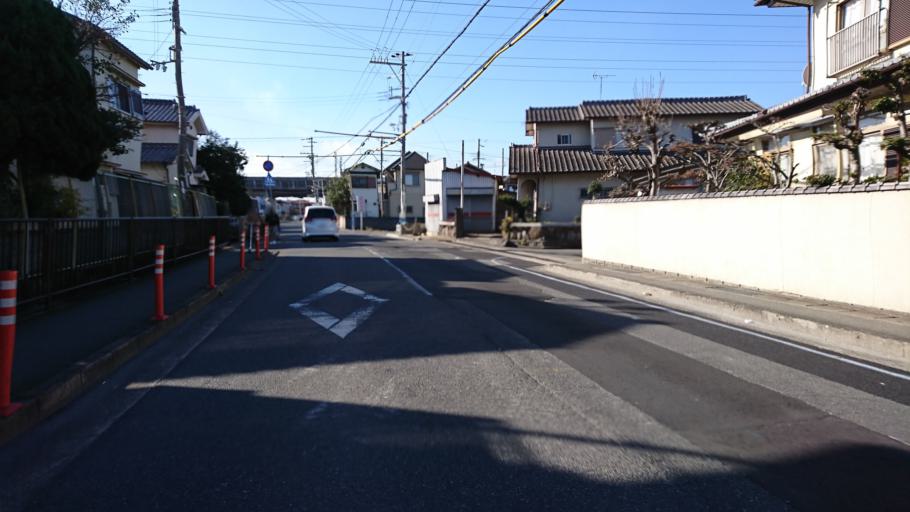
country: JP
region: Hyogo
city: Kakogawacho-honmachi
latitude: 34.7341
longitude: 134.8479
